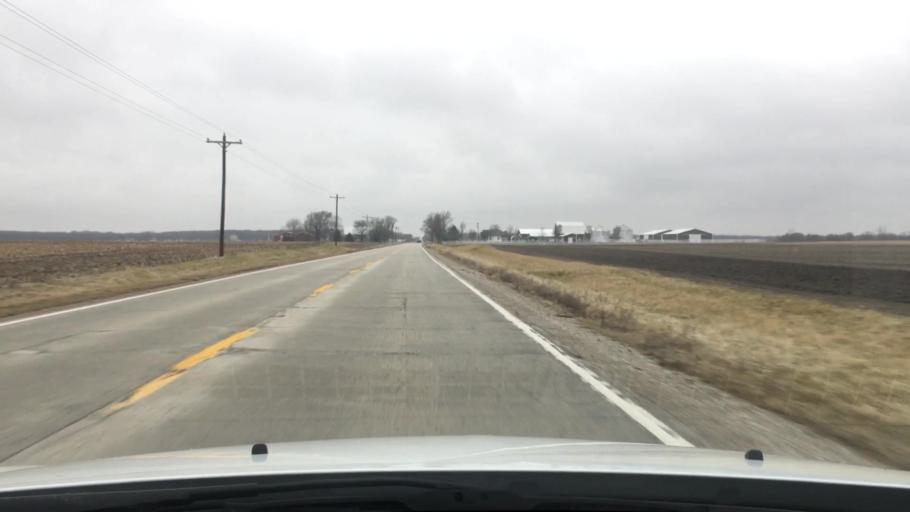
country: US
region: Illinois
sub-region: Iroquois County
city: Watseka
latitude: 40.8883
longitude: -87.8084
